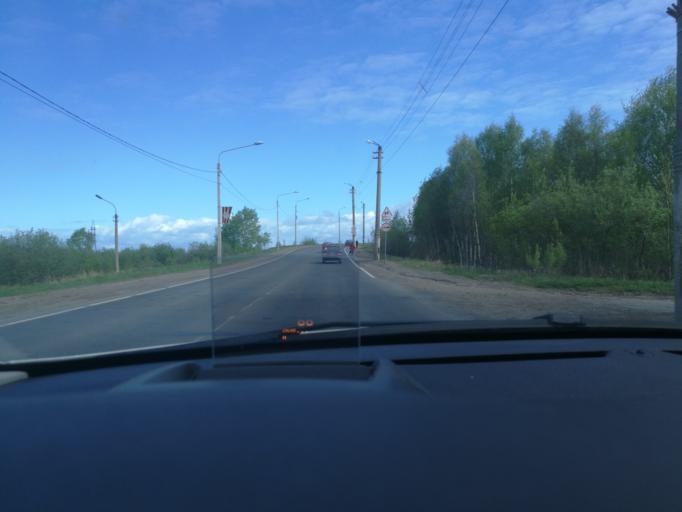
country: RU
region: Arkhangelskaya
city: Arkhangel'sk
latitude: 64.5984
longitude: 40.5503
